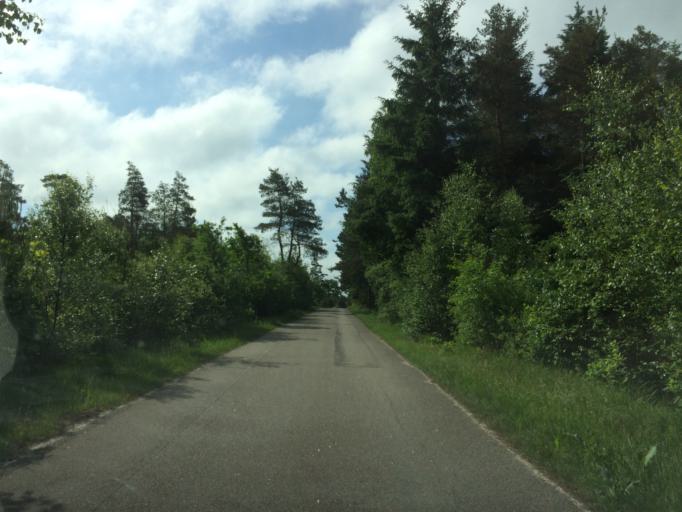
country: DK
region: Central Jutland
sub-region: Holstebro Kommune
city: Ulfborg
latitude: 56.2326
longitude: 8.4363
